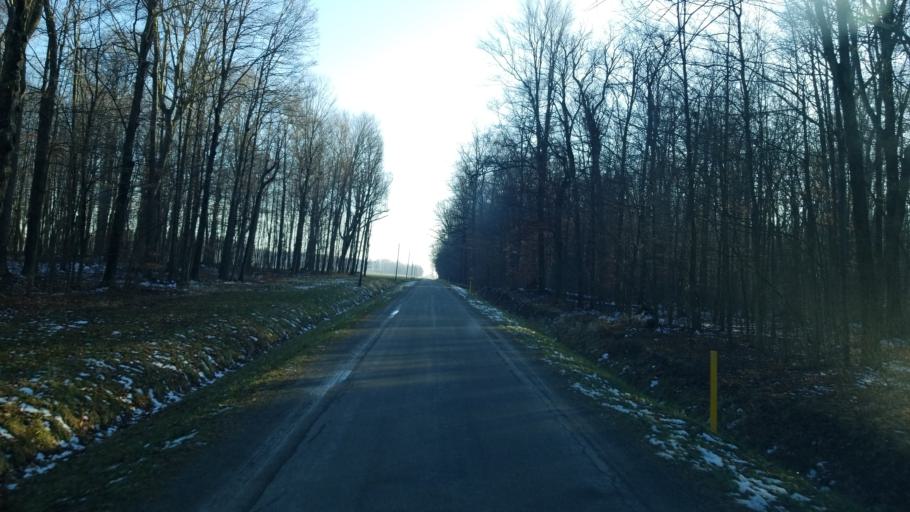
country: US
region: Ohio
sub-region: Crawford County
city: Bucyrus
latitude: 40.9256
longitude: -82.9210
